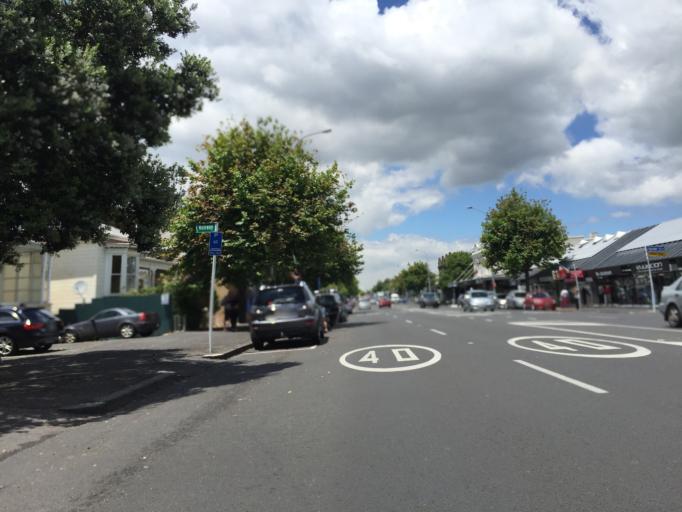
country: NZ
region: Auckland
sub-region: Auckland
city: Auckland
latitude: -36.8495
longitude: 174.7442
